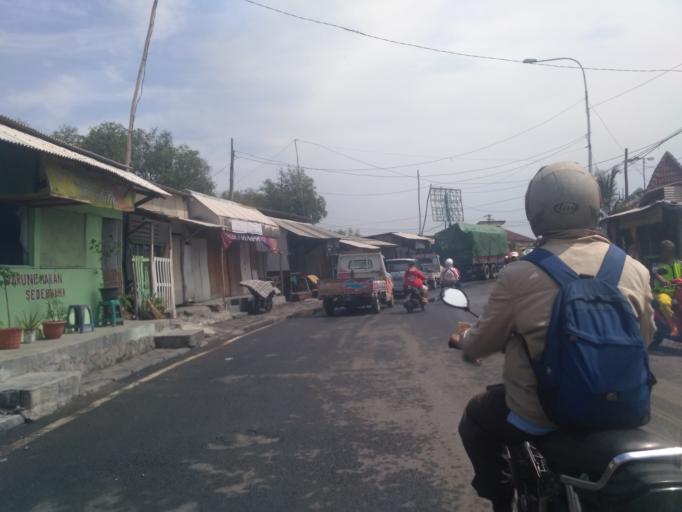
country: ID
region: Central Java
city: Semarang
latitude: -6.9568
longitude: 110.4208
